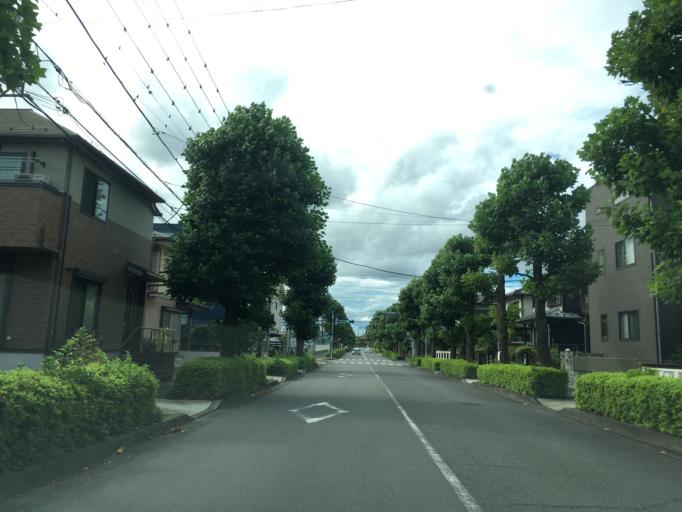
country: JP
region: Kanagawa
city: Minami-rinkan
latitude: 35.5073
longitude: 139.4694
